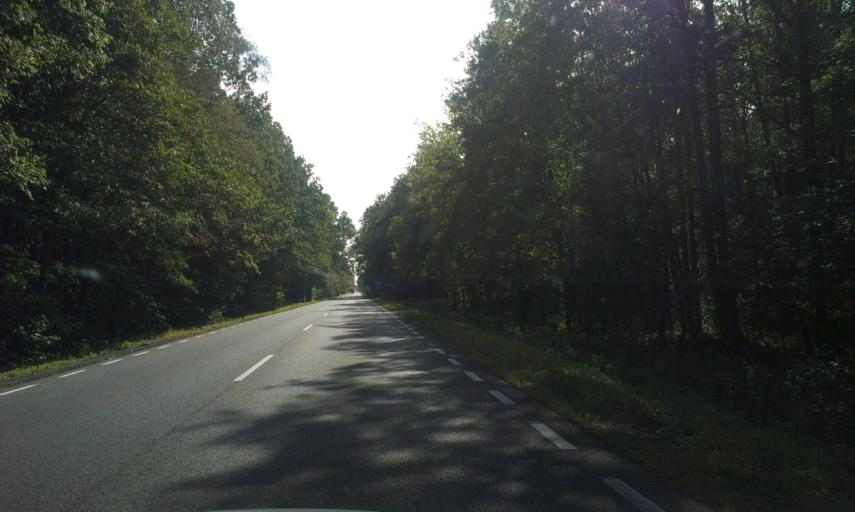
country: PL
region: West Pomeranian Voivodeship
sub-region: Powiat szczecinecki
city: Szczecinek
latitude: 53.6282
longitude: 16.7736
